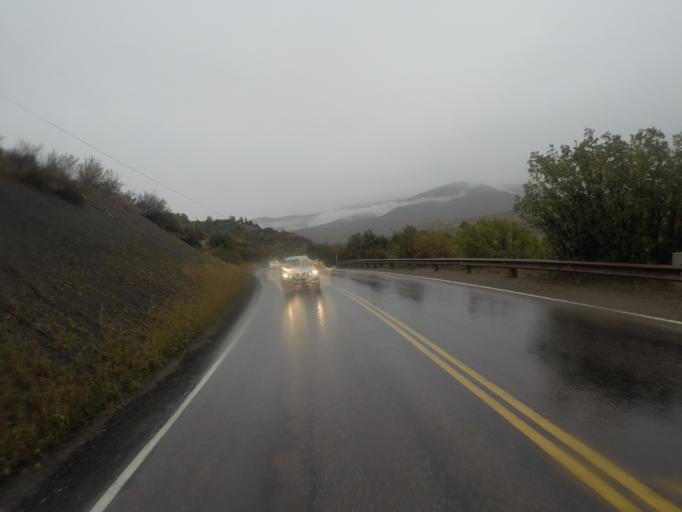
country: US
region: Colorado
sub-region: Pitkin County
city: Snowmass Village
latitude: 39.2457
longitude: -106.8890
